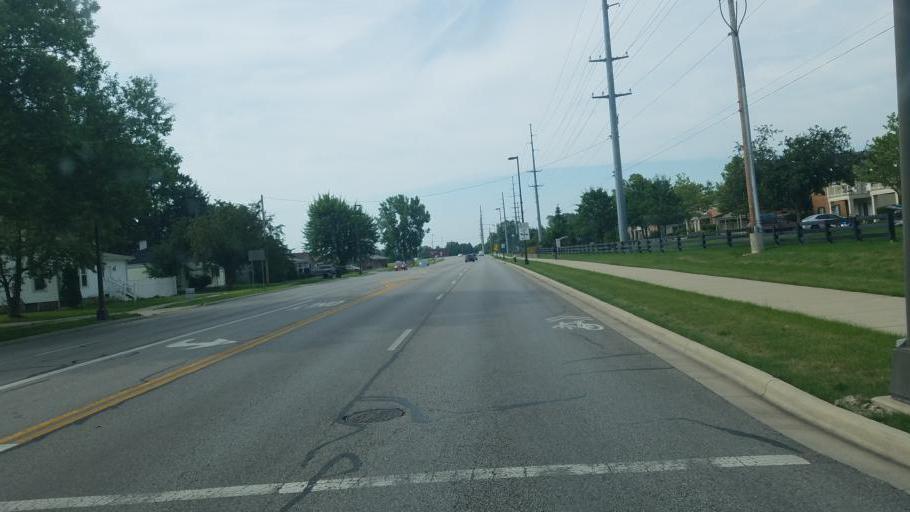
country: US
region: Ohio
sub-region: Franklin County
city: Hilliard
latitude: 40.0222
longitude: -83.1602
